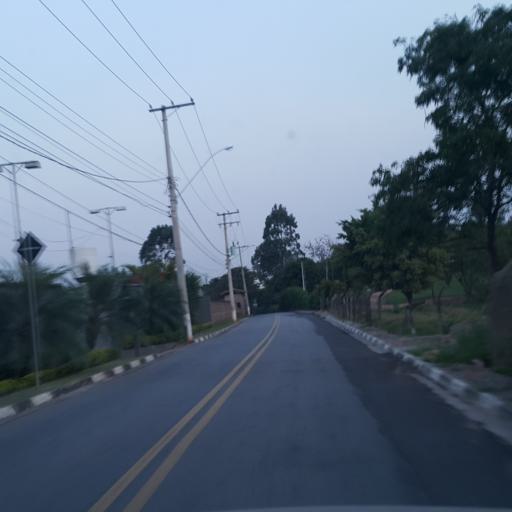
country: BR
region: Sao Paulo
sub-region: Louveira
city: Louveira
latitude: -23.0699
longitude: -46.9570
